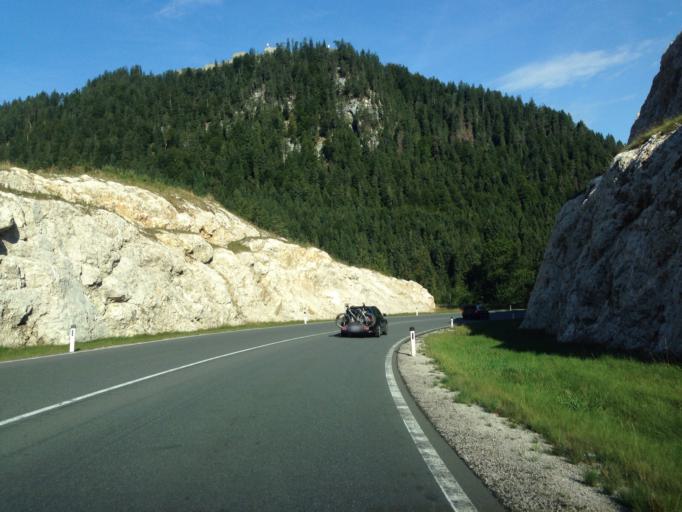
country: AT
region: Tyrol
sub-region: Politischer Bezirk Reutte
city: Ehenbichl
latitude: 47.4596
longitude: 10.7181
